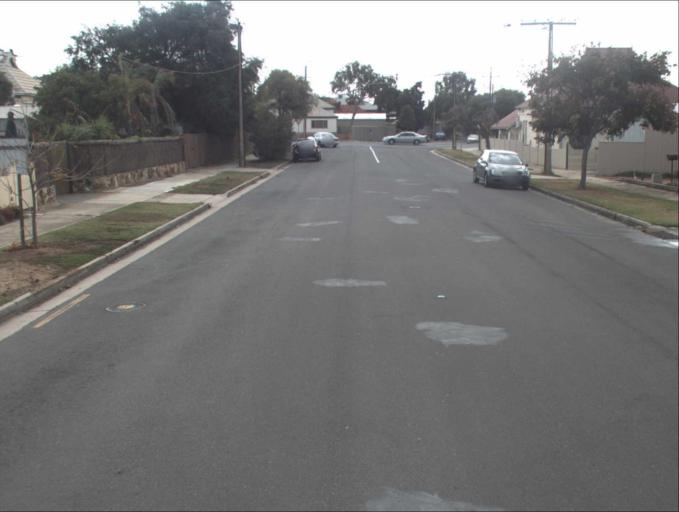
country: AU
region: South Australia
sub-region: Charles Sturt
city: West Lakes Shore
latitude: -34.8454
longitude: 138.4829
